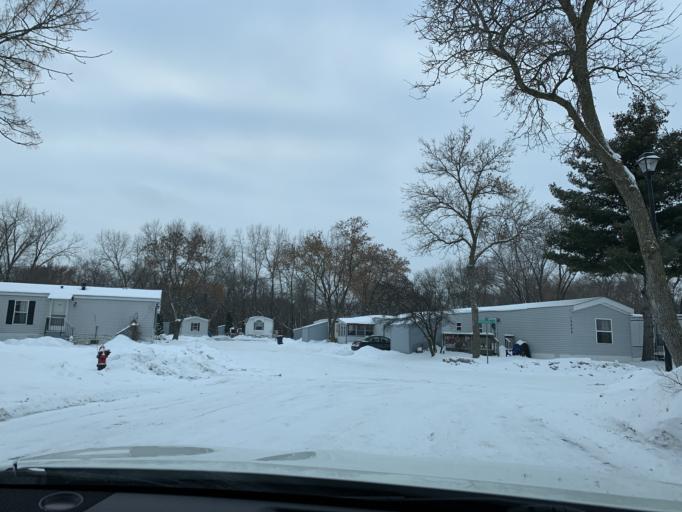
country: US
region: Minnesota
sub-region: Anoka County
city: Coon Rapids
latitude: 45.1595
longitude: -93.2951
